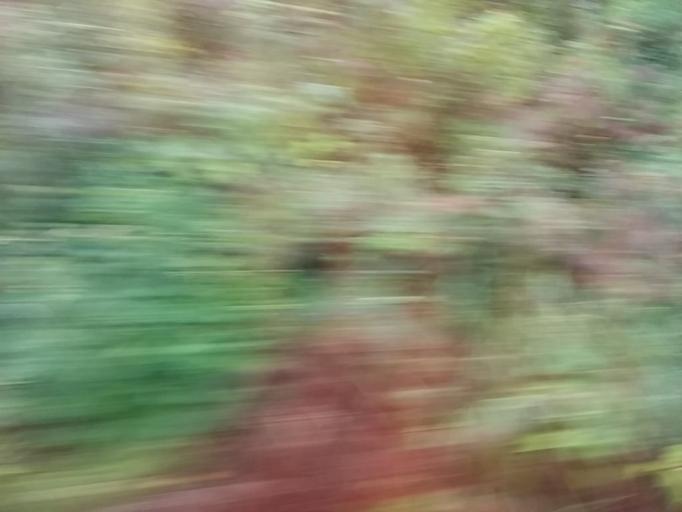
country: JP
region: Nara
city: Nara-shi
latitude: 34.7067
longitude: 135.7889
